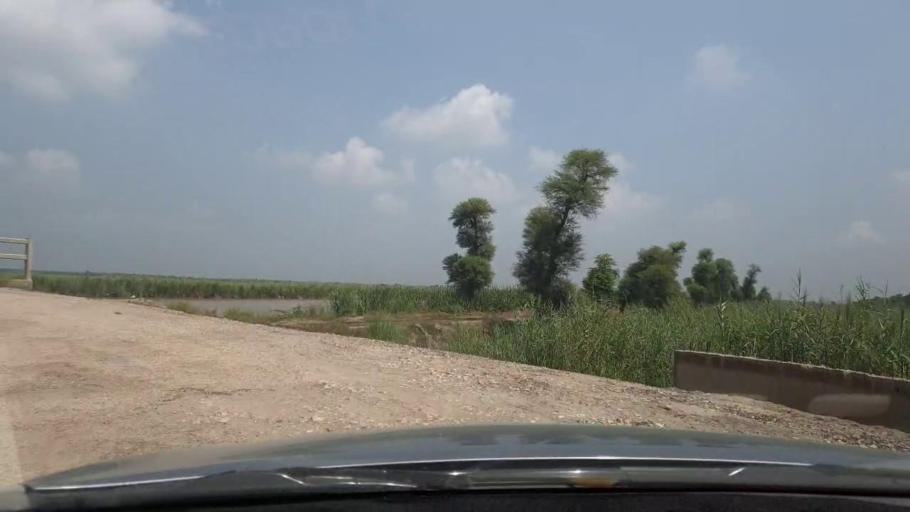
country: PK
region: Sindh
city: Khairpur
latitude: 27.4820
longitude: 68.7094
